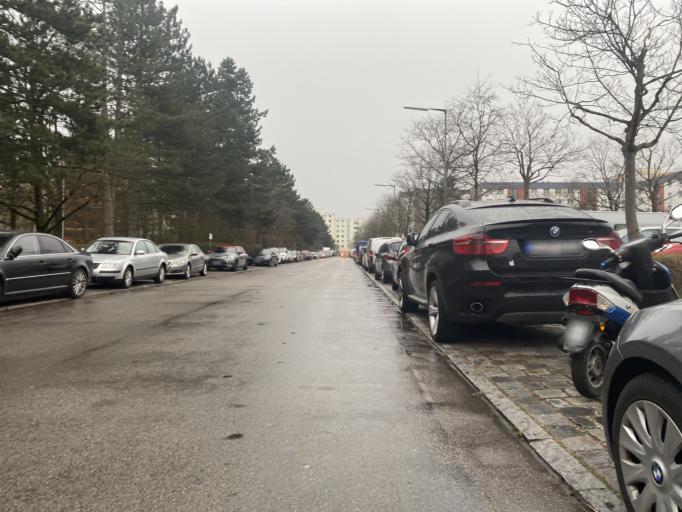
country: DE
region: Bavaria
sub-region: Upper Bavaria
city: Neubiberg
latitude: 48.1055
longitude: 11.6561
